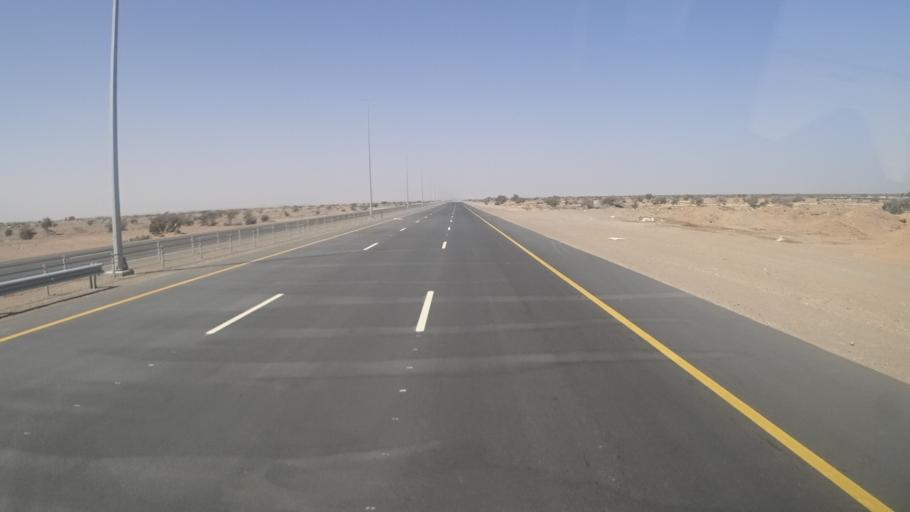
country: OM
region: Ash Sharqiyah
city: Sur
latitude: 22.2735
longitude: 59.2249
